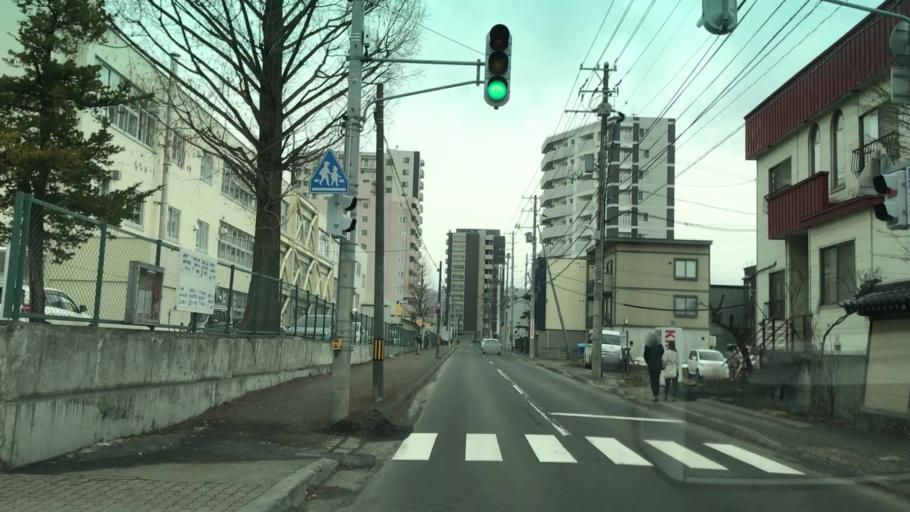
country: JP
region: Hokkaido
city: Sapporo
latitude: 43.0757
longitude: 141.2994
